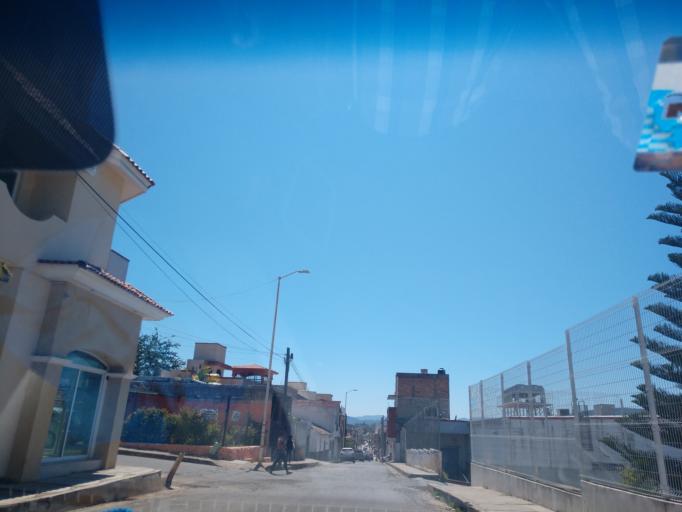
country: MX
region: Nayarit
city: Compostela
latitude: 21.2399
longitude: -104.8993
